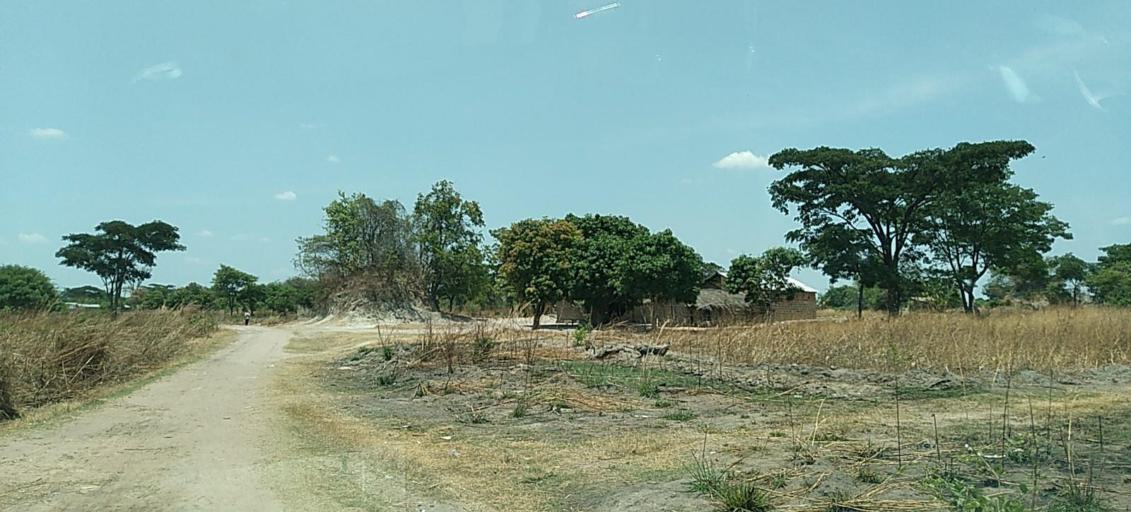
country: ZM
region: Copperbelt
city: Luanshya
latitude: -13.0742
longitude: 28.4051
